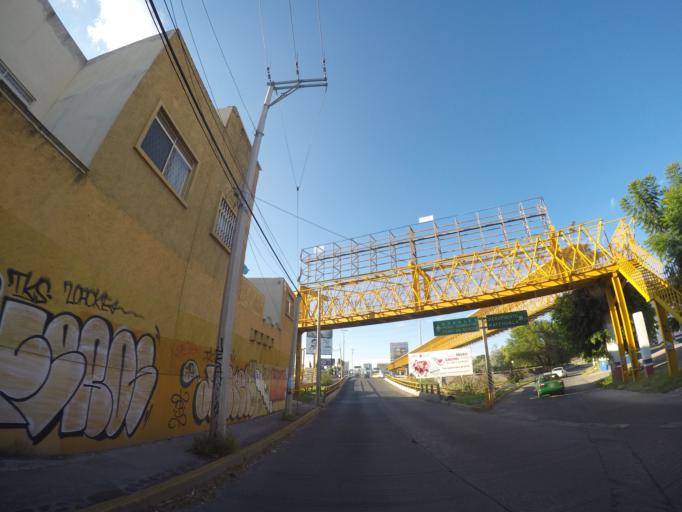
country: MX
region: San Luis Potosi
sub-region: San Luis Potosi
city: San Luis Potosi
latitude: 22.1576
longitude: -101.0000
